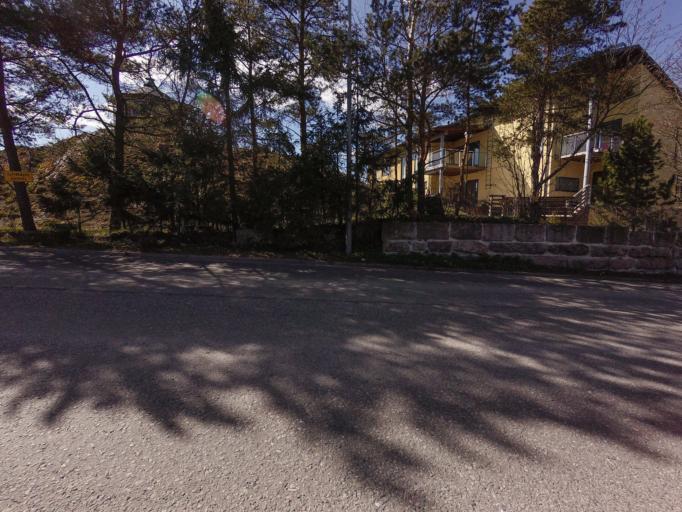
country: FI
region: Uusimaa
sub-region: Helsinki
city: Helsinki
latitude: 60.1583
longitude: 25.0494
